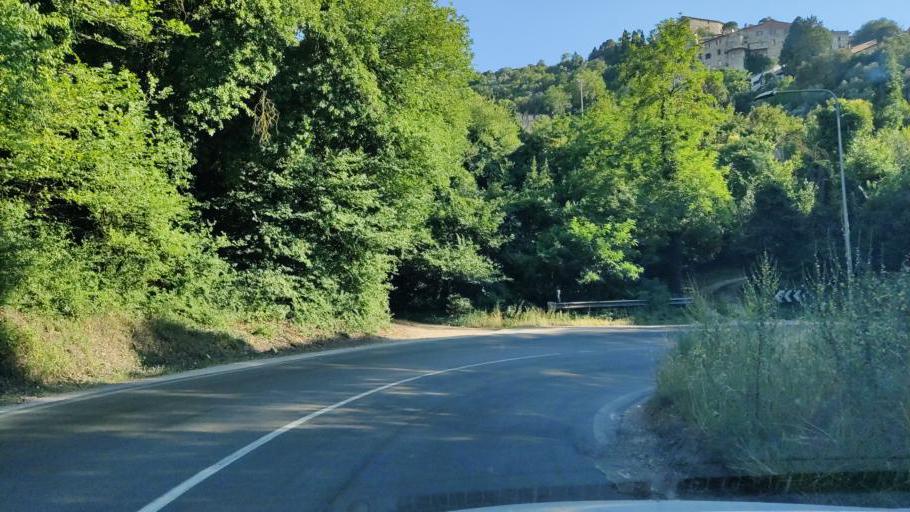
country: IT
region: Umbria
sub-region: Provincia di Terni
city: Narni
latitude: 42.5197
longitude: 12.5217
